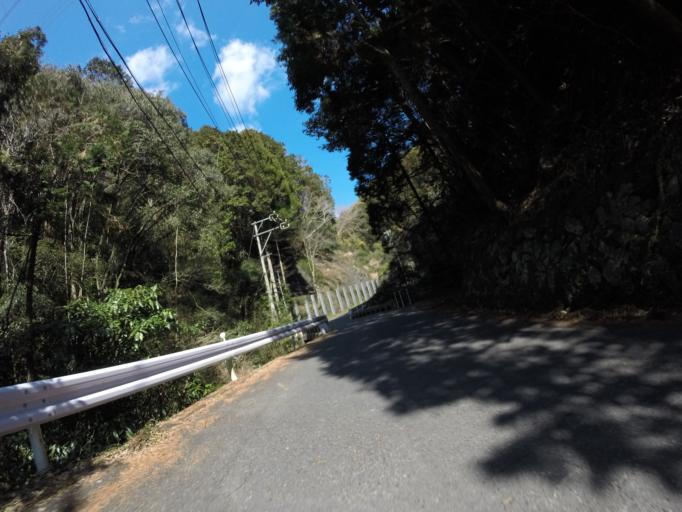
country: JP
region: Shizuoka
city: Shizuoka-shi
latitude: 35.0798
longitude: 138.4758
